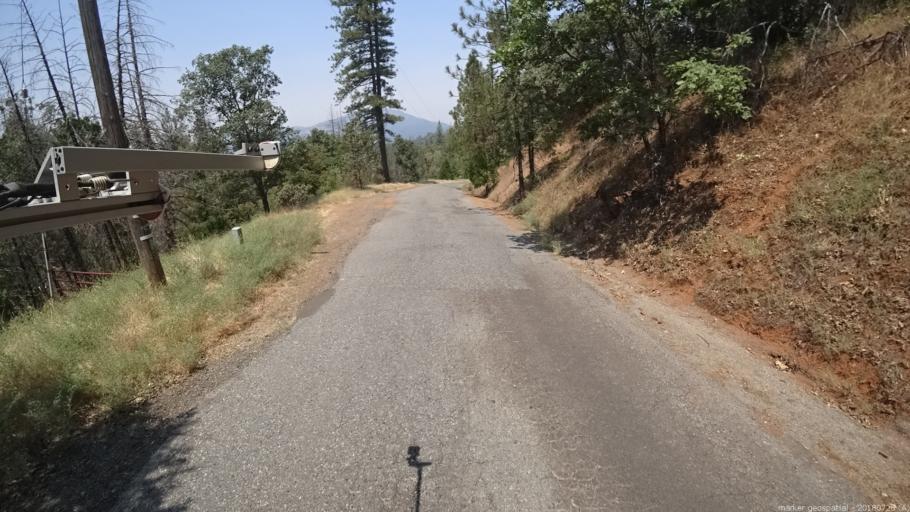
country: US
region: California
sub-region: Madera County
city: Oakhurst
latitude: 37.2775
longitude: -119.6296
